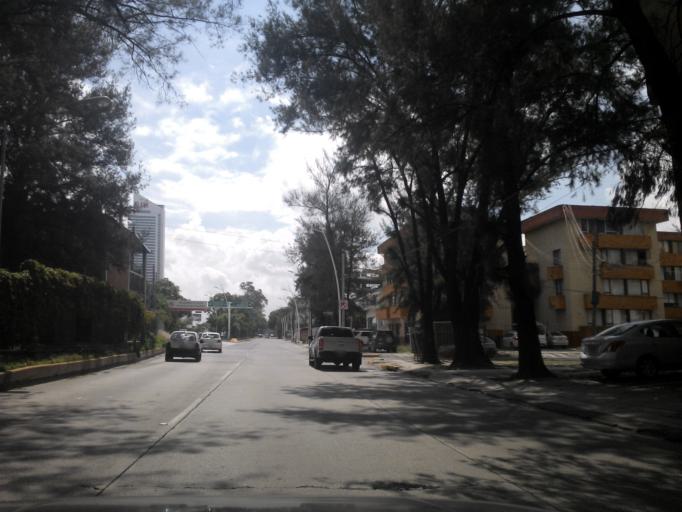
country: MX
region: Jalisco
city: Guadalajara
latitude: 20.6683
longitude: -103.4008
